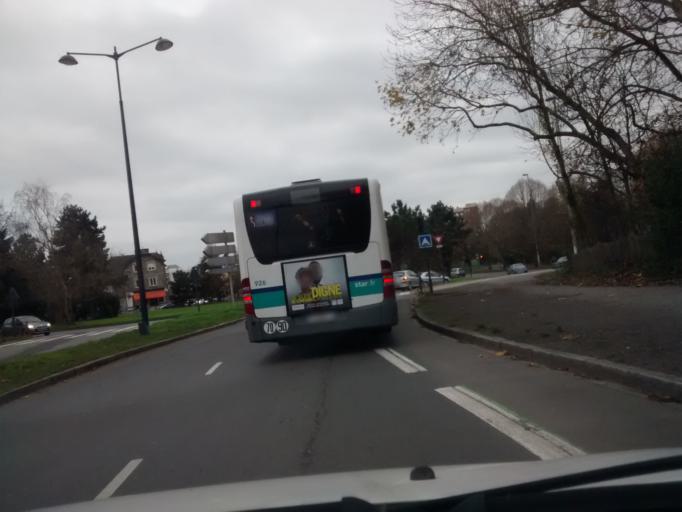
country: FR
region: Brittany
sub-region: Departement d'Ille-et-Vilaine
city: Rennes
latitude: 48.1278
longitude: -1.6509
